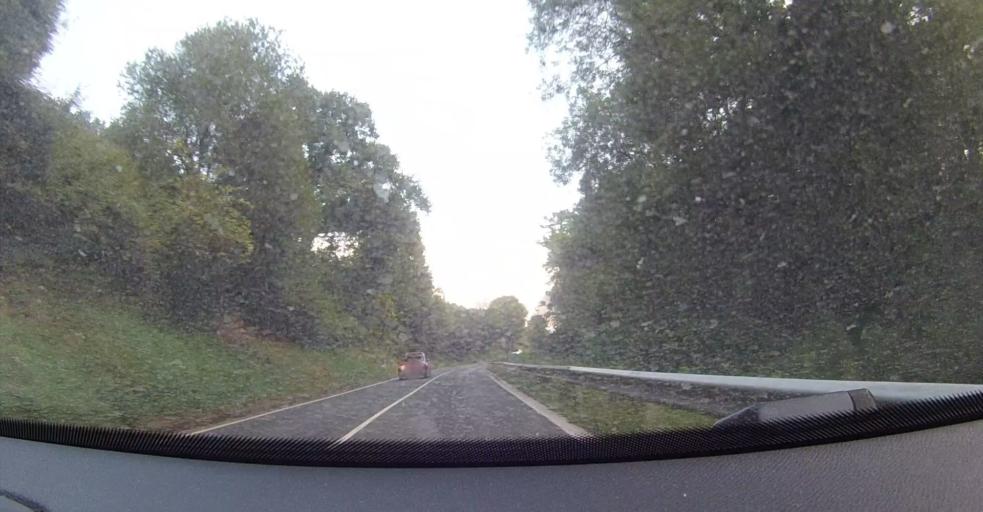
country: ES
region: Basque Country
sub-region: Bizkaia
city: Urrestieta
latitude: 43.2363
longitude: -3.1583
